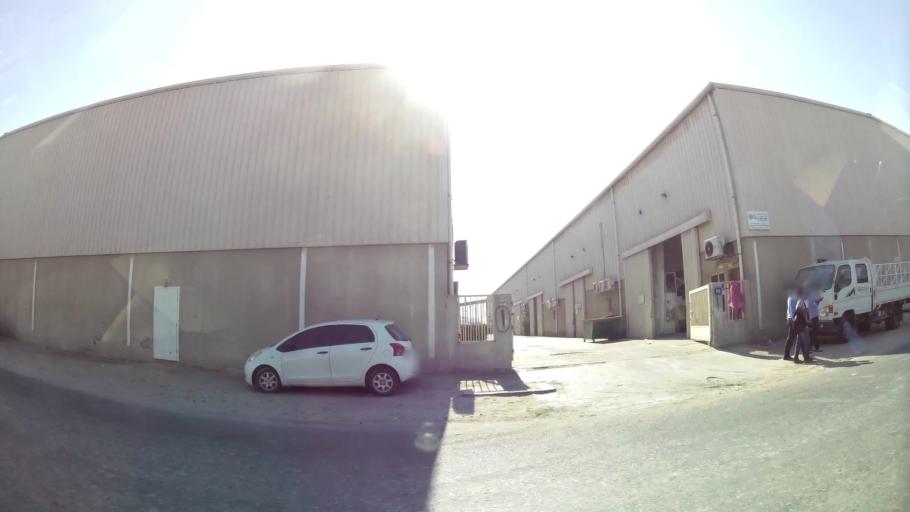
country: AE
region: Dubai
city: Dubai
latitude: 24.9923
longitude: 55.0990
